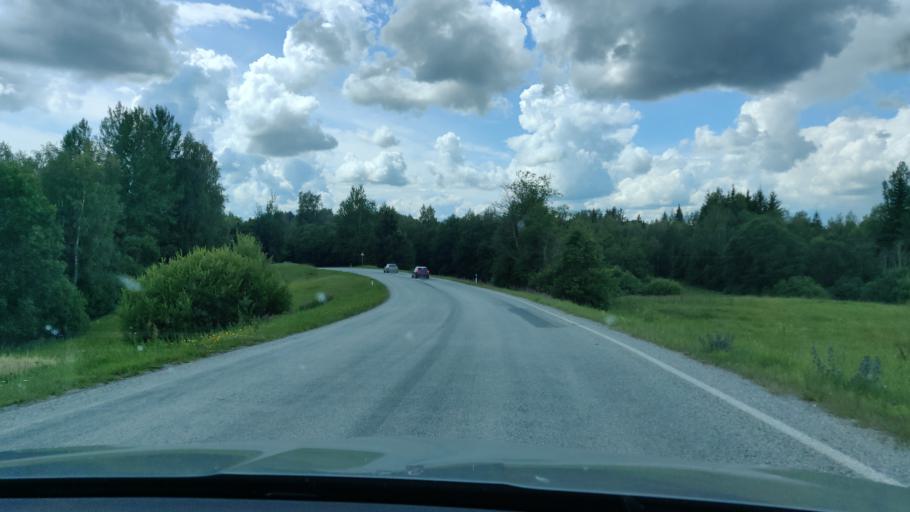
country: EE
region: Vorumaa
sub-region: Antsla vald
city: Vana-Antsla
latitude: 58.0249
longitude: 26.5060
